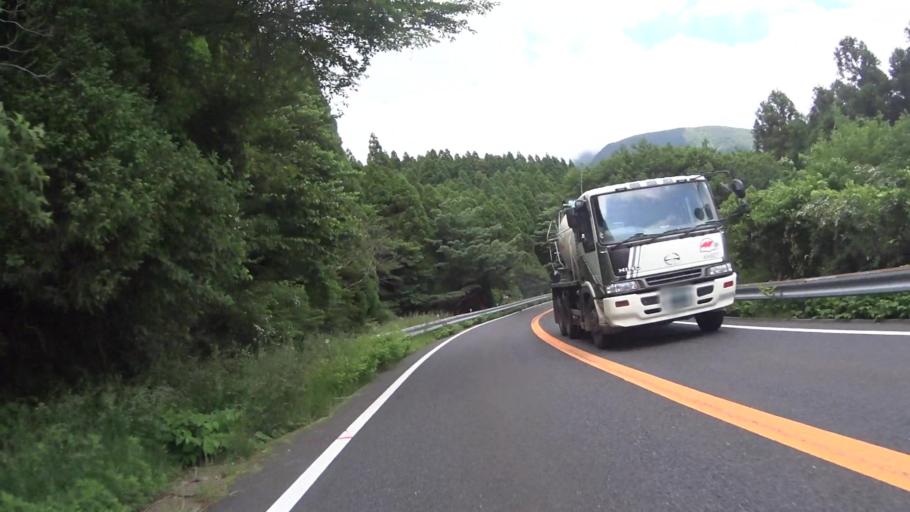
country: JP
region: Kumamoto
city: Aso
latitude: 33.0824
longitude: 131.1913
